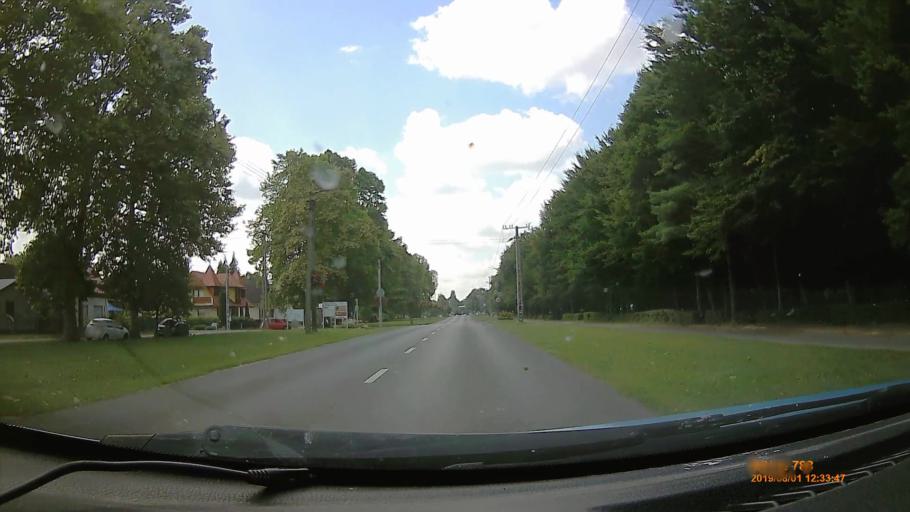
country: HU
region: Baranya
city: Harkany
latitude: 45.8511
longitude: 18.2479
